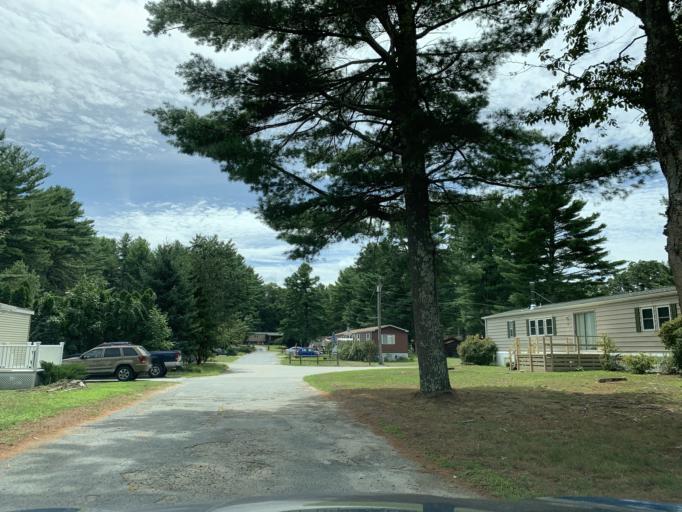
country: US
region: Rhode Island
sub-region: Washington County
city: Exeter
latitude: 41.5523
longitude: -71.6188
